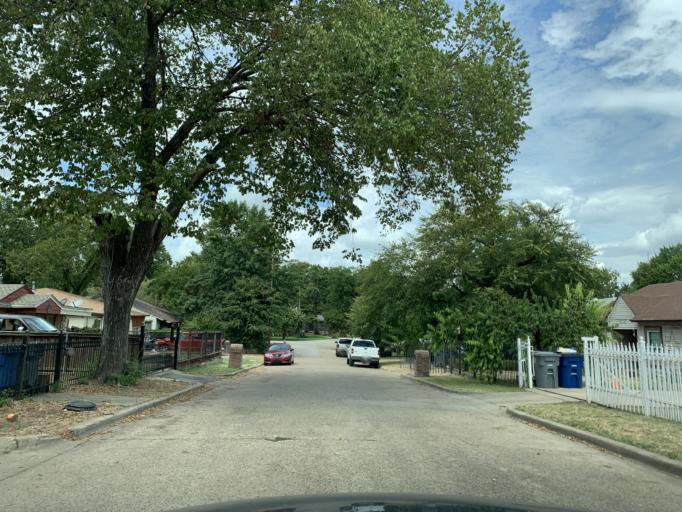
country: US
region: Texas
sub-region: Dallas County
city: Cockrell Hill
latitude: 32.7387
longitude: -96.8781
